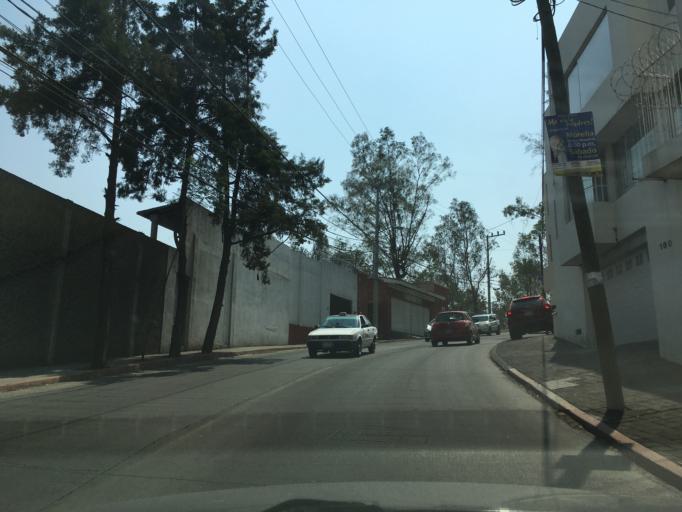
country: MX
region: Michoacan
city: Morelia
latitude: 19.6785
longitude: -101.1879
